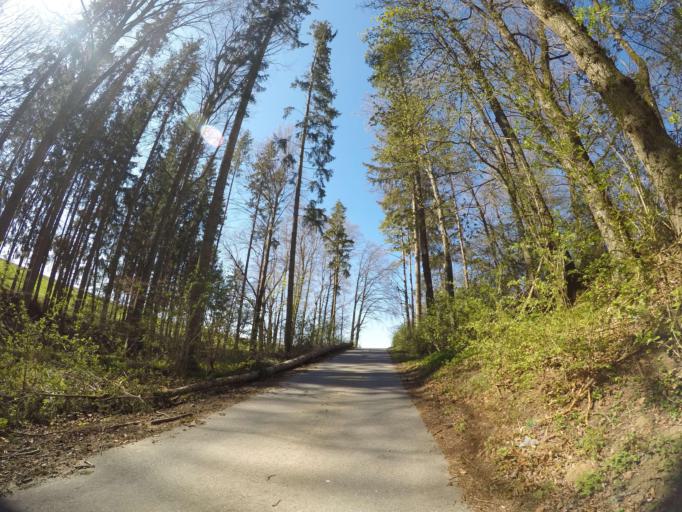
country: DE
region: Baden-Wuerttemberg
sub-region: Tuebingen Region
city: Guggenhausen
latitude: 47.8768
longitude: 9.4552
